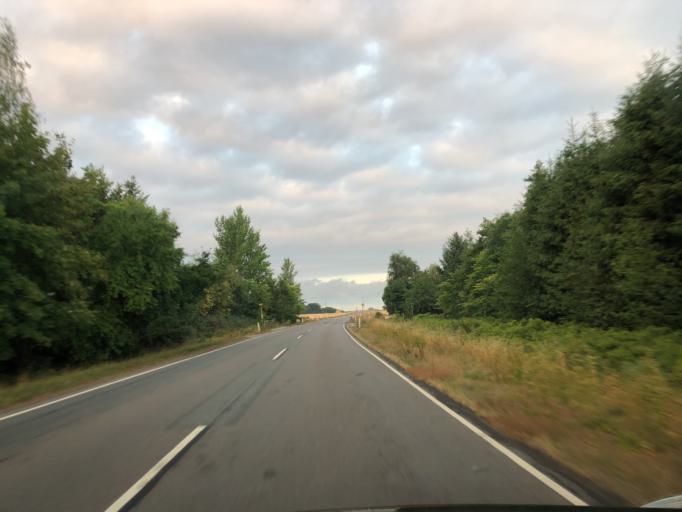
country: DK
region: Zealand
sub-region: Soro Kommune
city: Dianalund
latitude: 55.4555
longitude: 11.4436
